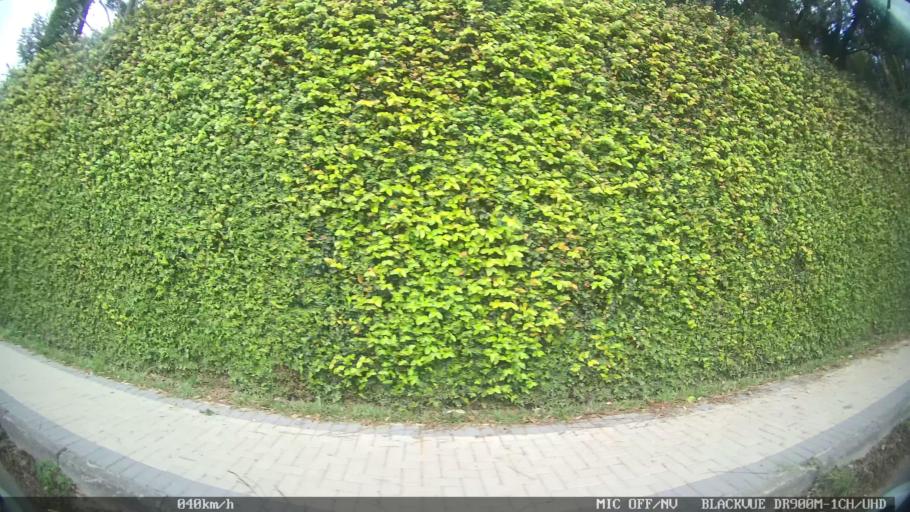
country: BR
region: Parana
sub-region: Colombo
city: Colombo
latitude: -25.3571
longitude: -49.2346
